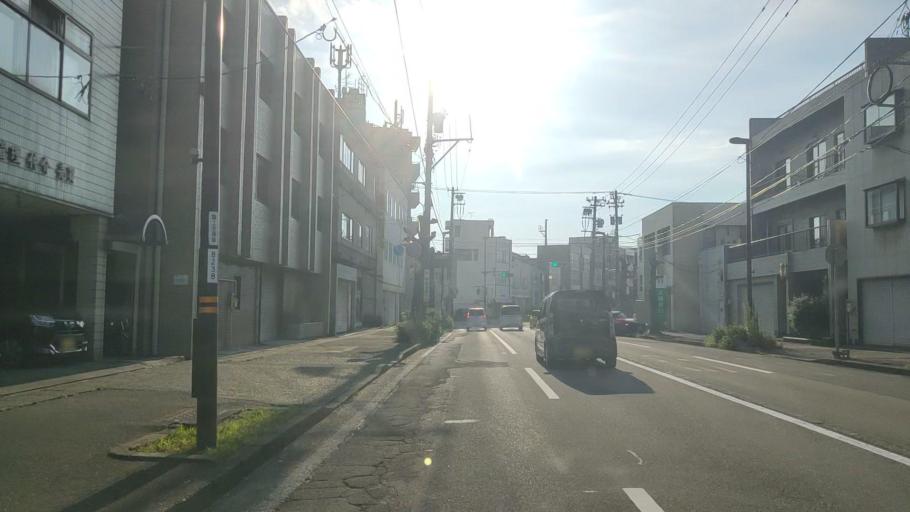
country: JP
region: Ishikawa
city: Kanazawa-shi
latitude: 36.5637
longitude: 136.6686
